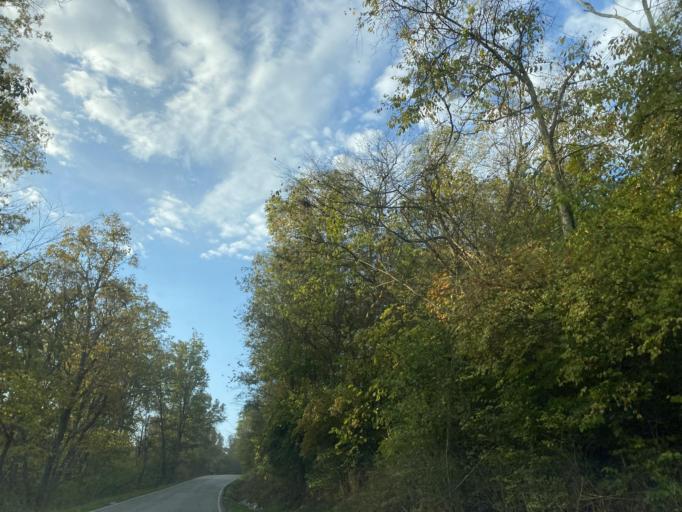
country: US
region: Kentucky
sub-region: Pendleton County
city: Falmouth
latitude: 38.7691
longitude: -84.3382
